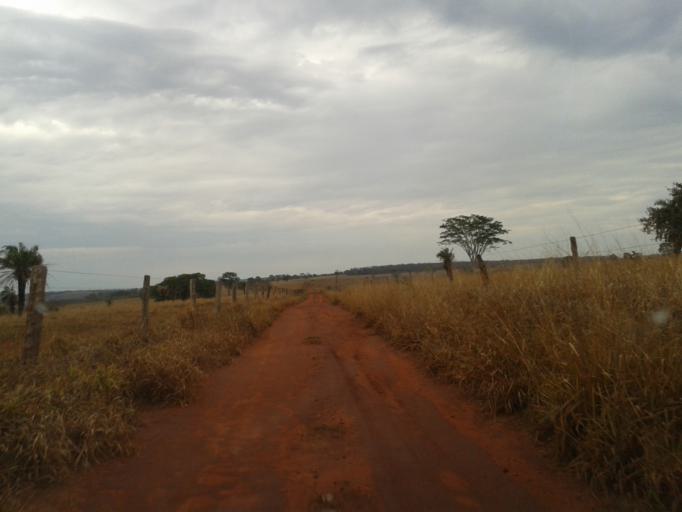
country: BR
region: Minas Gerais
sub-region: Santa Vitoria
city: Santa Vitoria
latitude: -18.8701
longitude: -49.8146
